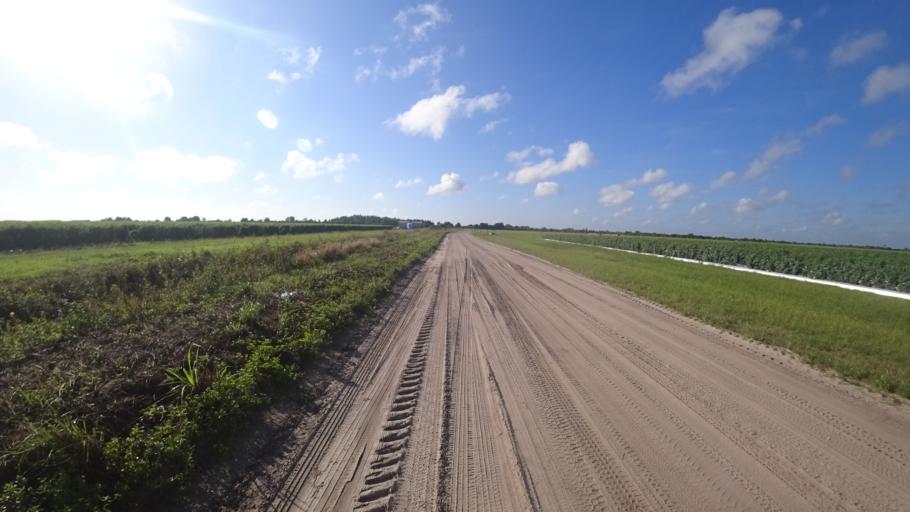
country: US
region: Florida
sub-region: Hillsborough County
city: Wimauma
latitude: 27.5356
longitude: -82.3179
